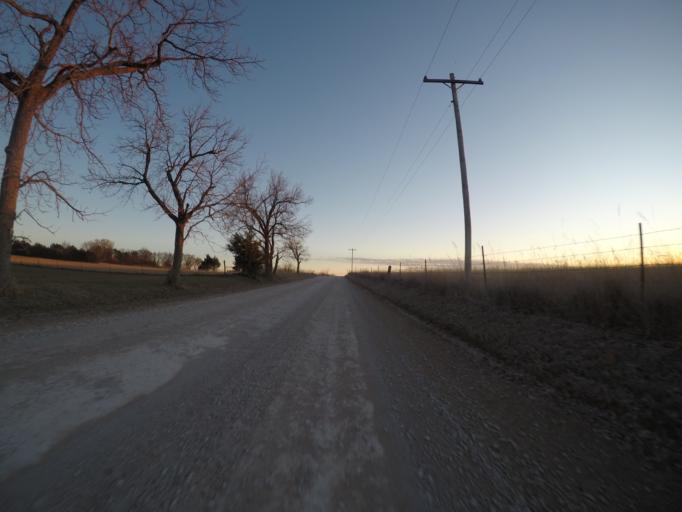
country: US
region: Kansas
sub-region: Riley County
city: Manhattan
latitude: 39.2447
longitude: -96.4826
